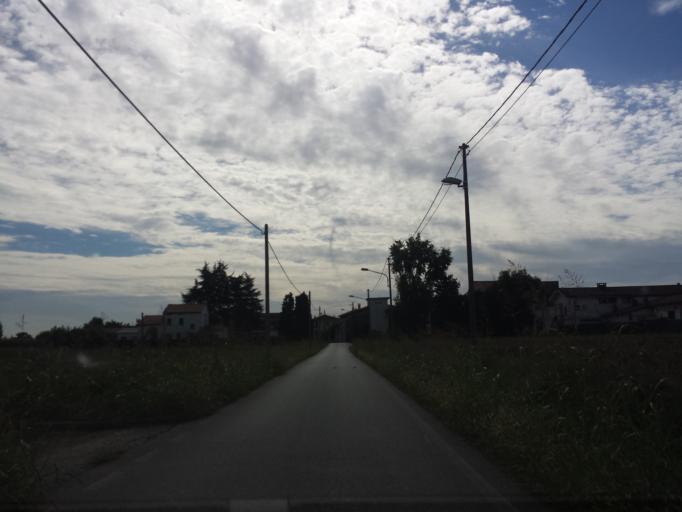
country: IT
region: Veneto
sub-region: Provincia di Vicenza
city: Vicenza
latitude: 45.5624
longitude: 11.5712
